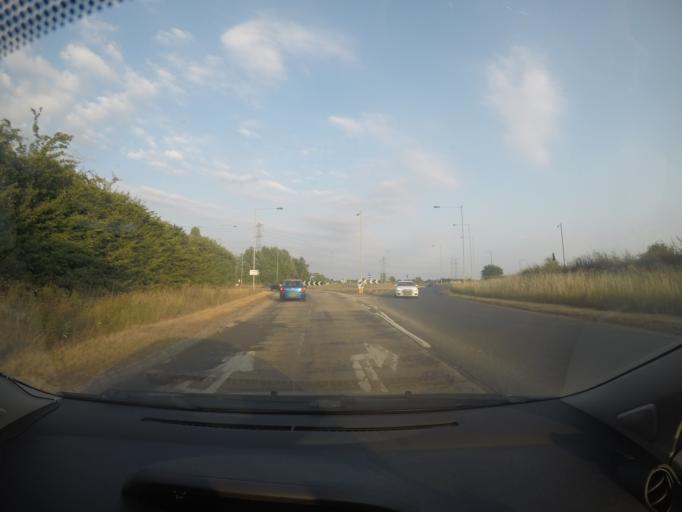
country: GB
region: England
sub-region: City of York
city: Huntington
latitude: 53.9995
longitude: -1.0437
